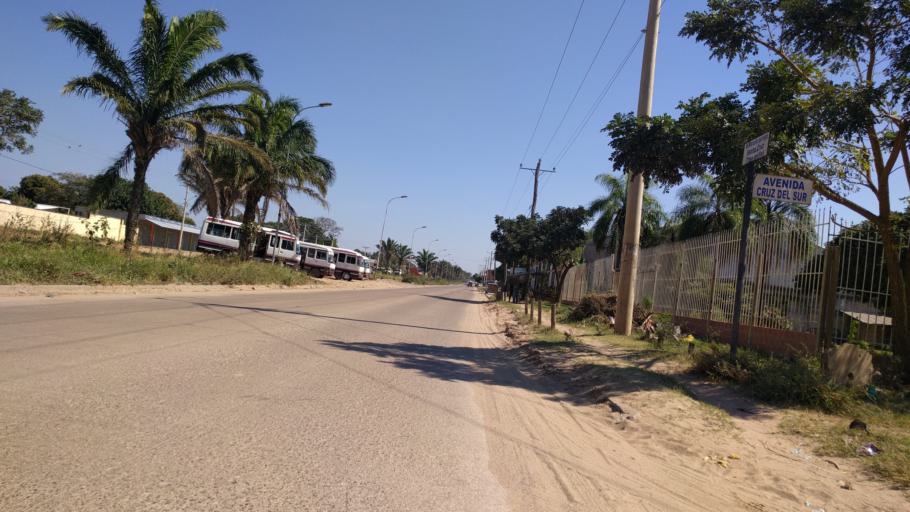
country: BO
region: Santa Cruz
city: Santa Cruz de la Sierra
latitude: -17.8470
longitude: -63.2073
